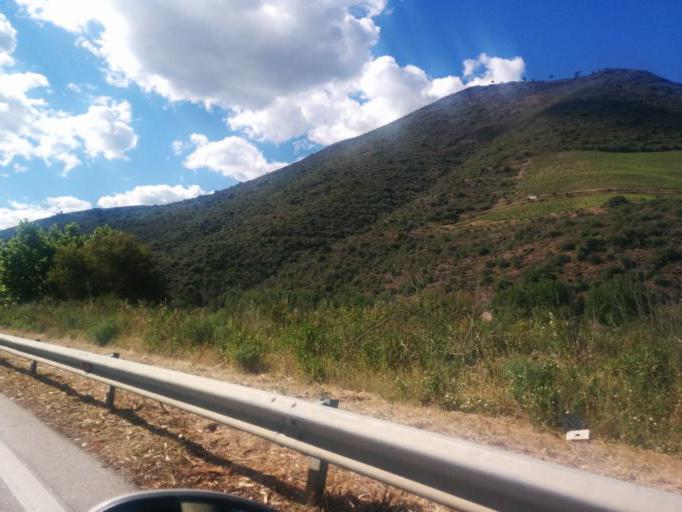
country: PT
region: Viseu
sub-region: Armamar
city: Armamar
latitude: 41.1420
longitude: -7.7045
